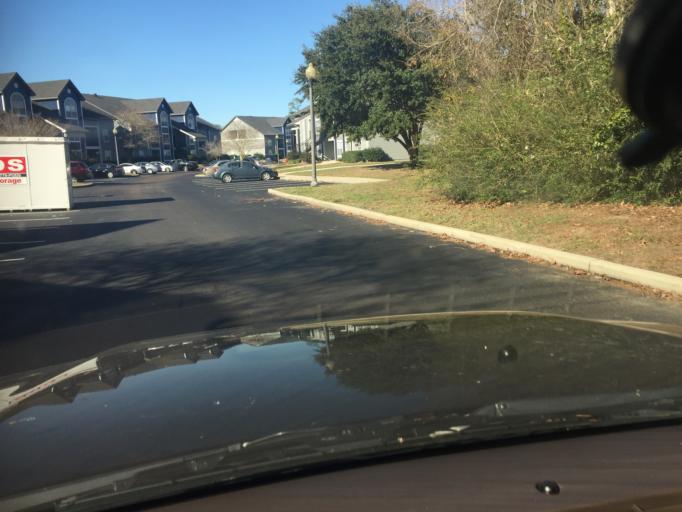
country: US
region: Louisiana
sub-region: Saint Tammany Parish
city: Slidell
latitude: 30.3131
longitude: -89.7468
